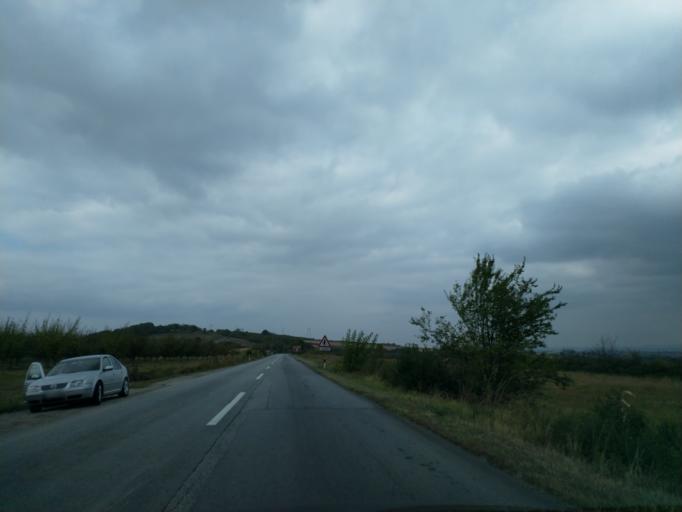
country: RS
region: Central Serbia
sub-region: Sumadijski Okrug
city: Topola
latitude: 44.1576
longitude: 20.7386
